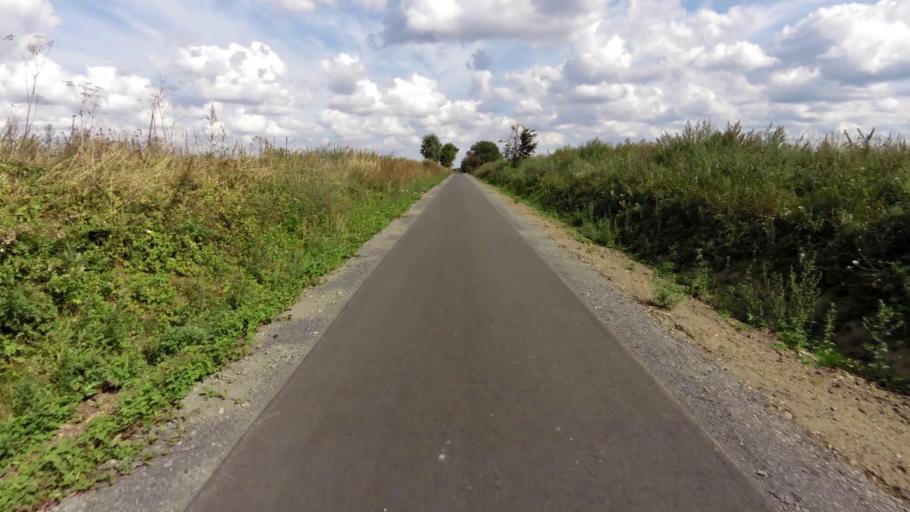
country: PL
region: West Pomeranian Voivodeship
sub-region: Powiat mysliborski
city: Barlinek
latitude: 52.9856
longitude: 15.1322
